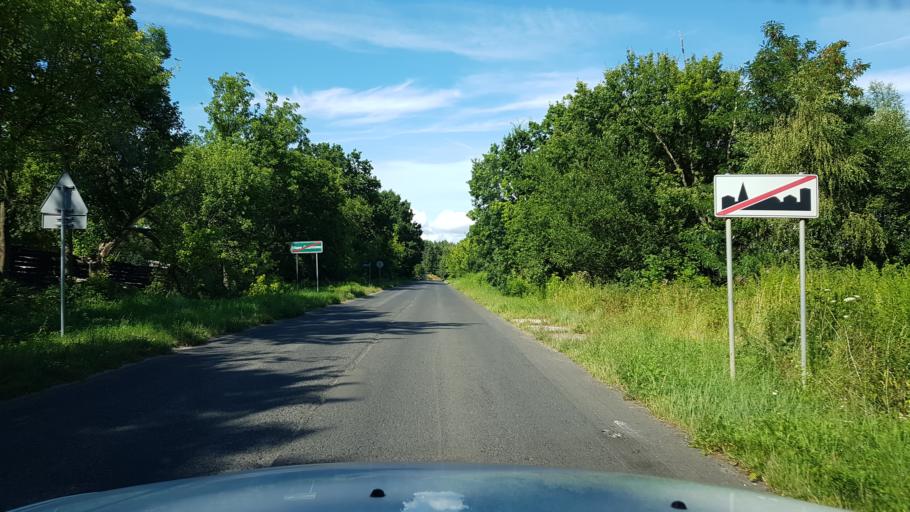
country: PL
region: West Pomeranian Voivodeship
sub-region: Powiat gryfinski
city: Stare Czarnowo
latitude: 53.2923
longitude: 14.7853
